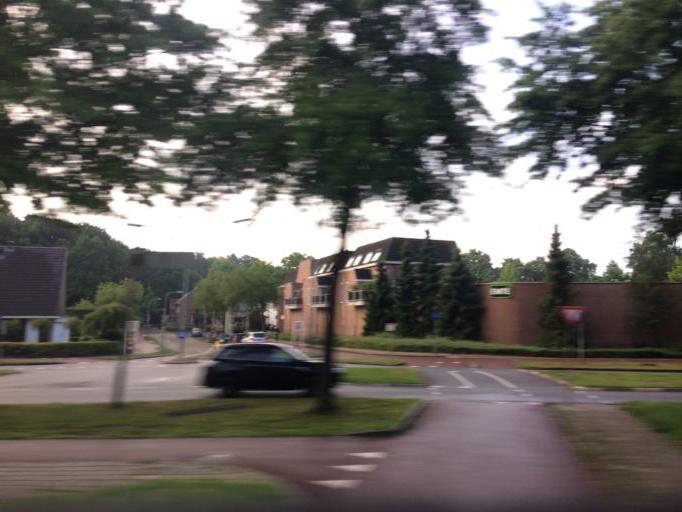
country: NL
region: Gelderland
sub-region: Gemeente Wijchen
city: Wijchen
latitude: 51.8103
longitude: 5.7241
